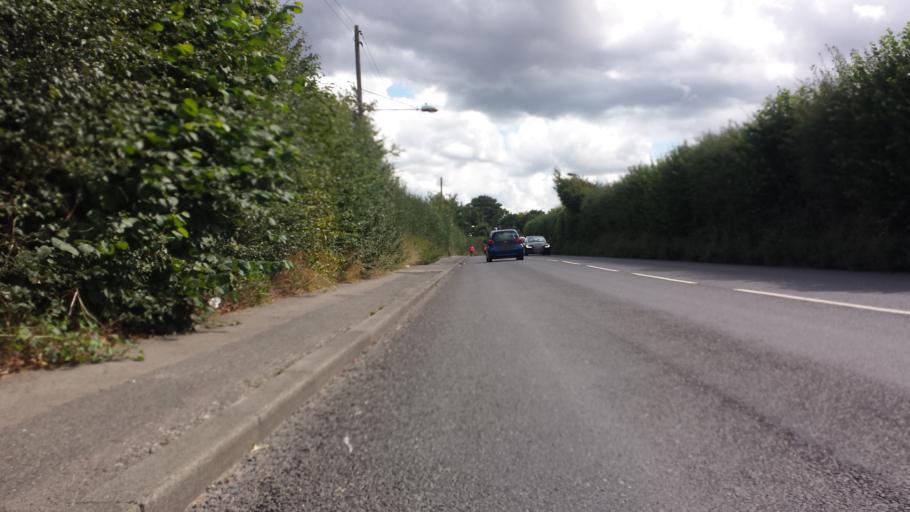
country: GB
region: England
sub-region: Kent
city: Swanley
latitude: 51.4062
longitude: 0.1836
